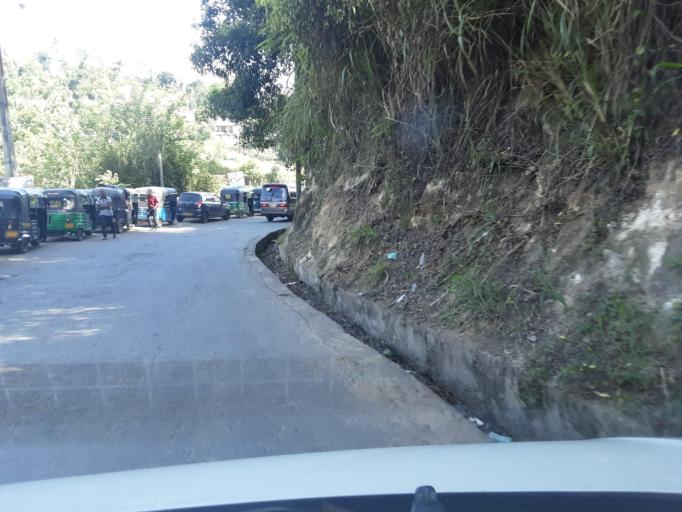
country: LK
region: Uva
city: Haputale
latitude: 6.9022
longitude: 80.9127
